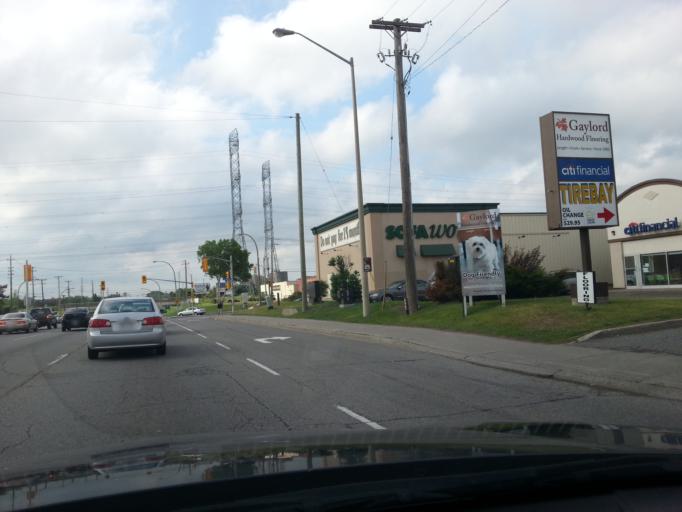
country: CA
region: Ontario
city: Ottawa
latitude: 45.3374
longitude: -75.7255
